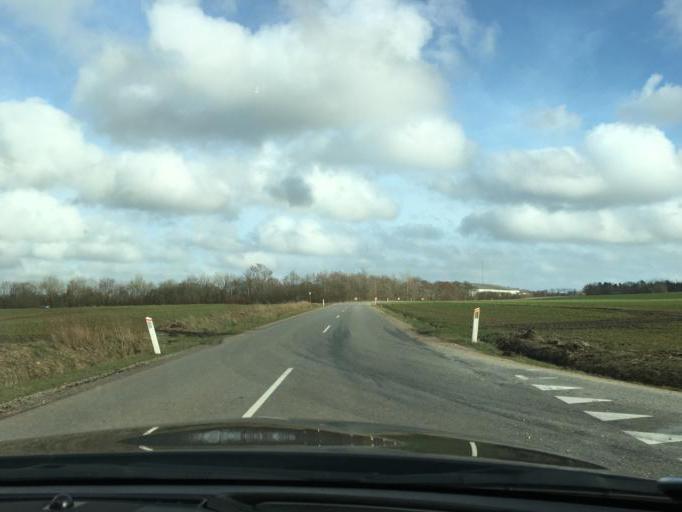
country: DK
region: South Denmark
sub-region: Esbjerg Kommune
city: Tjaereborg
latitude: 55.5703
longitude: 8.5834
